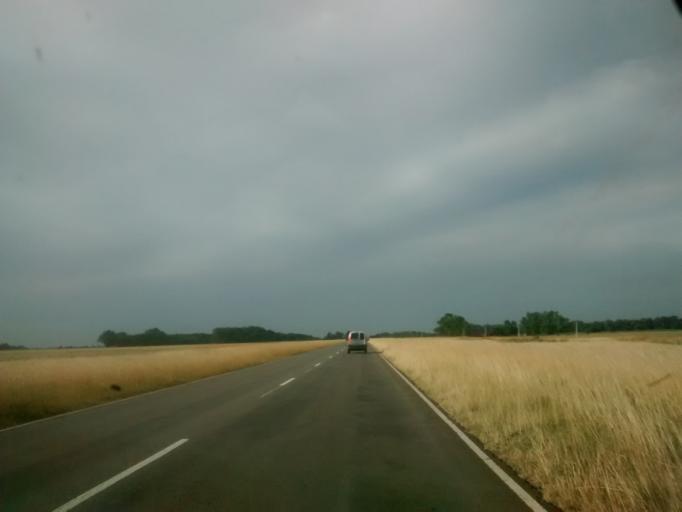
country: AR
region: Buenos Aires
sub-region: Partido de Ayacucho
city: Ayacucho
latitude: -36.6703
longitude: -58.5745
